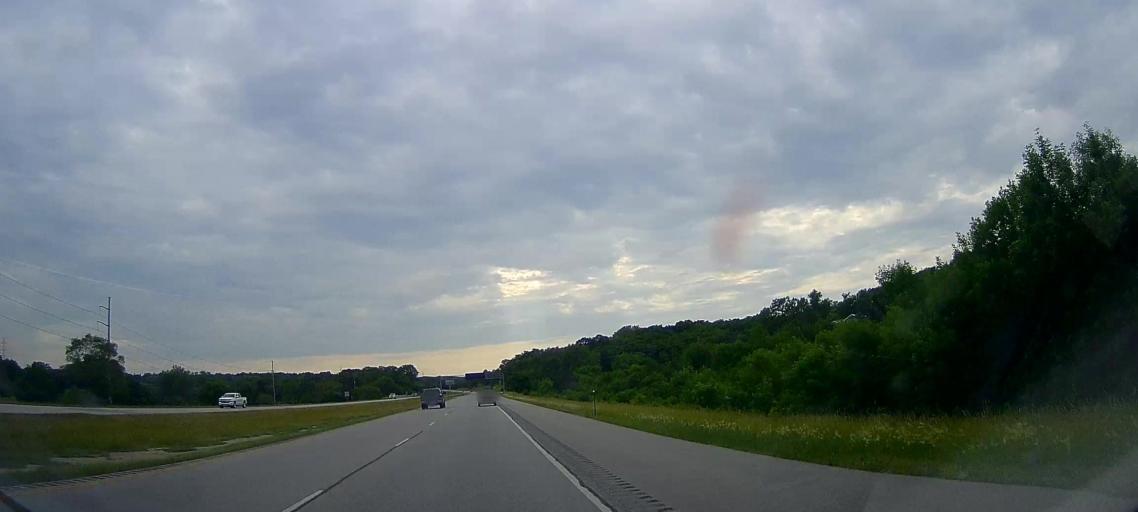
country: US
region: Iowa
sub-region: Pottawattamie County
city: Carter Lake
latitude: 41.3464
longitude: -96.0016
